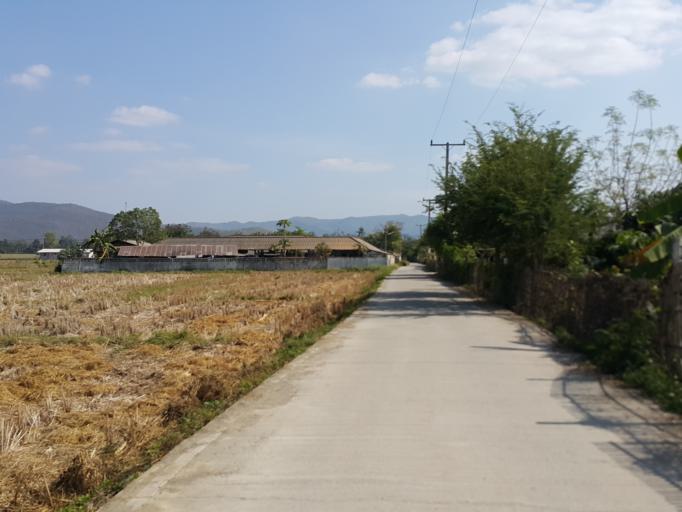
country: TH
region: Chiang Mai
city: San Kamphaeng
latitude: 18.8034
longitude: 99.1686
